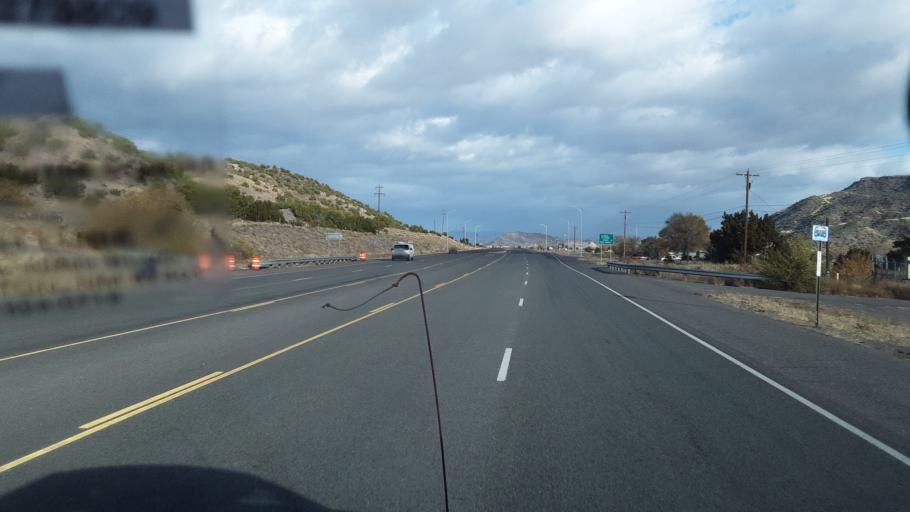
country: US
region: New Mexico
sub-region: Rio Arriba County
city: Ohkay Owingeh
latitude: 36.0699
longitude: -106.1236
